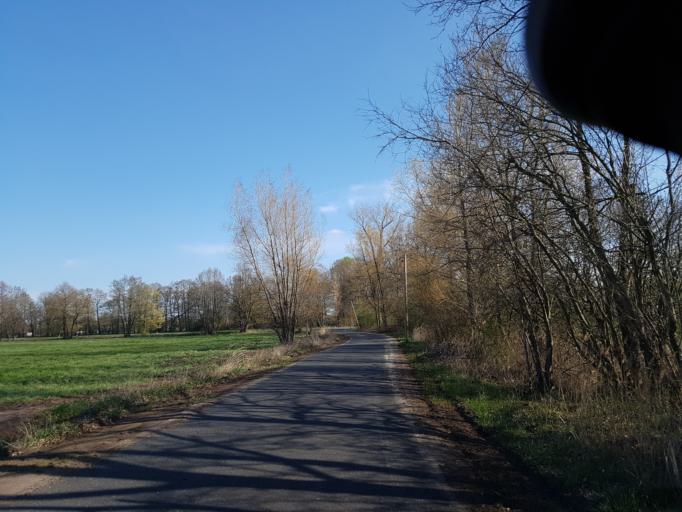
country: DE
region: Brandenburg
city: Schilda
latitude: 51.6333
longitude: 13.3093
